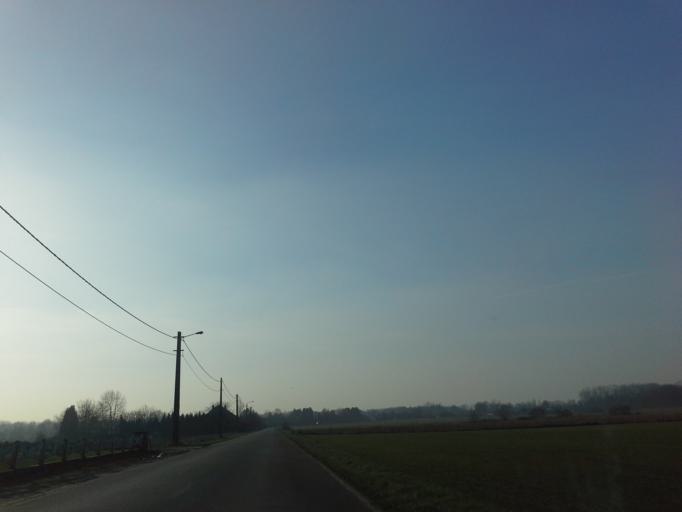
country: BE
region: Flanders
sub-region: Provincie Antwerpen
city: Geel
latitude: 51.1572
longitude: 5.0360
